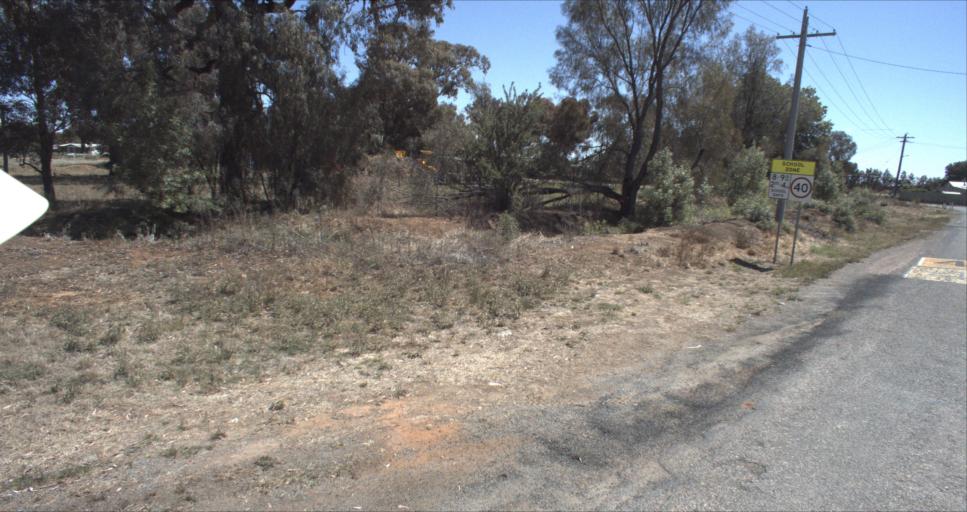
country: AU
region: New South Wales
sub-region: Leeton
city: Leeton
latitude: -34.5257
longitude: 146.3325
